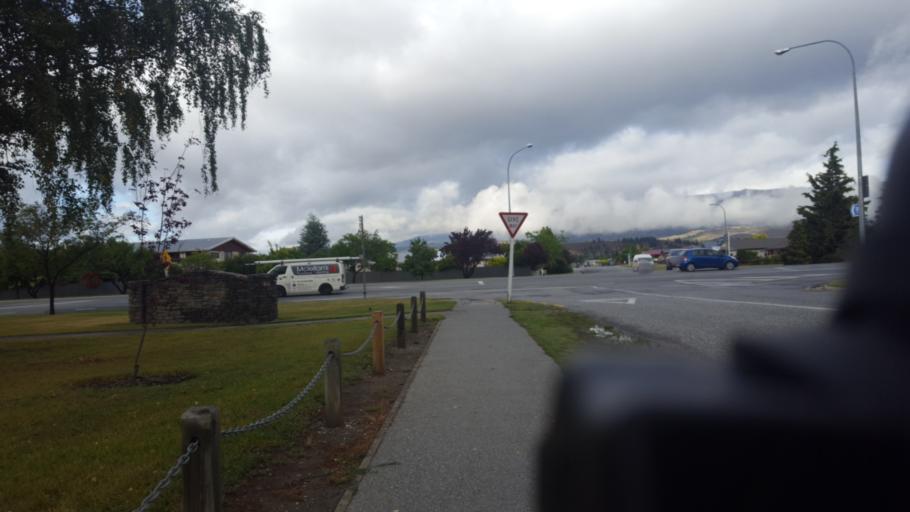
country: NZ
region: Otago
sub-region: Queenstown-Lakes District
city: Wanaka
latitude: -45.2442
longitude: 169.3799
